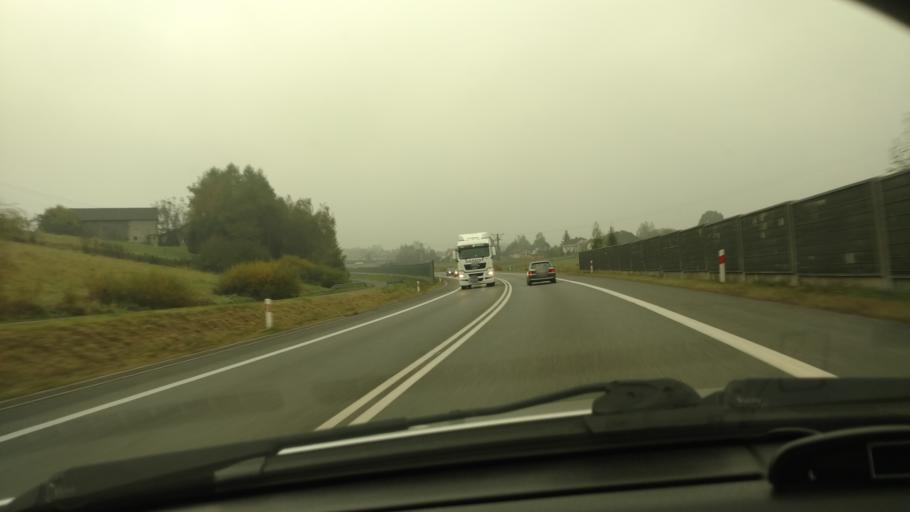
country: PL
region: Lesser Poland Voivodeship
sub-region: Powiat gorlicki
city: Biecz
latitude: 49.7190
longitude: 21.2515
